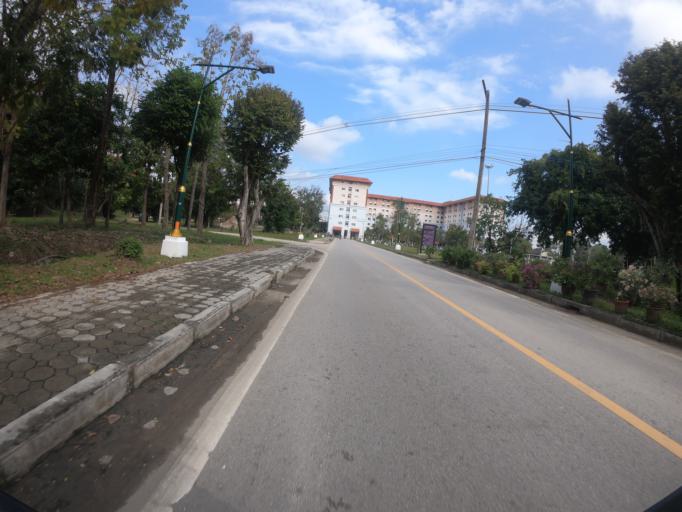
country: TH
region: Chiang Mai
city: Chiang Mai
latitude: 18.7977
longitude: 98.9585
